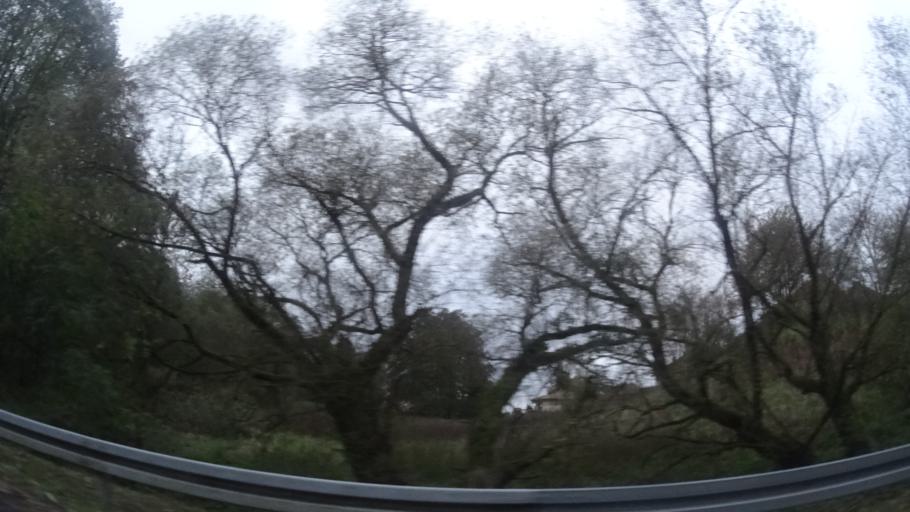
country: DE
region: Hesse
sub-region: Regierungsbezirk Giessen
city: Freiensteinau
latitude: 50.3989
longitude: 9.4243
